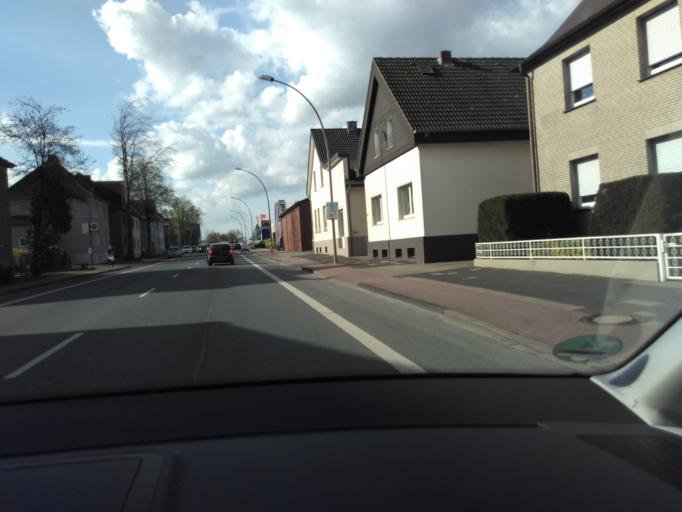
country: DE
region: North Rhine-Westphalia
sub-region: Regierungsbezirk Munster
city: Beckum
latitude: 51.7711
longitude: 8.0389
